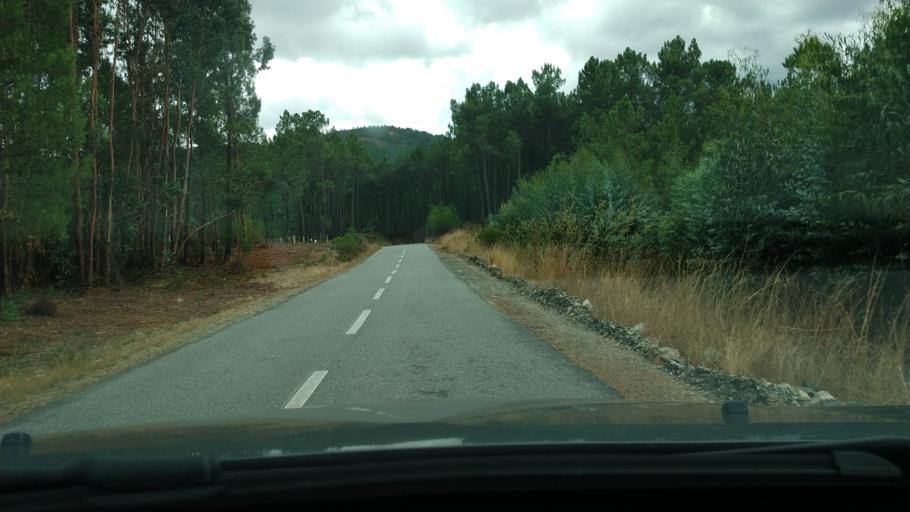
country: PT
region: Castelo Branco
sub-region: Concelho do Fundao
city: Aldeia de Joanes
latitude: 40.2196
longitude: -7.6310
